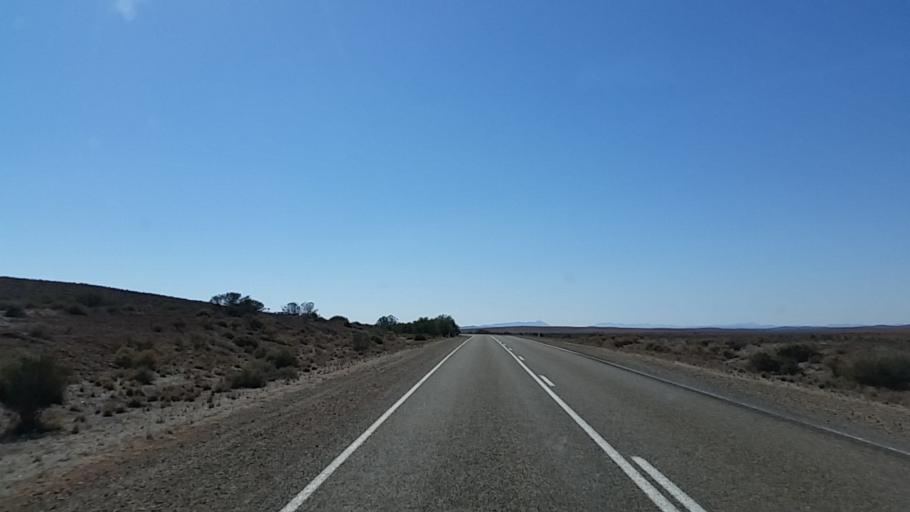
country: AU
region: South Australia
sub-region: Flinders Ranges
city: Quorn
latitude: -32.1332
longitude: 138.5133
